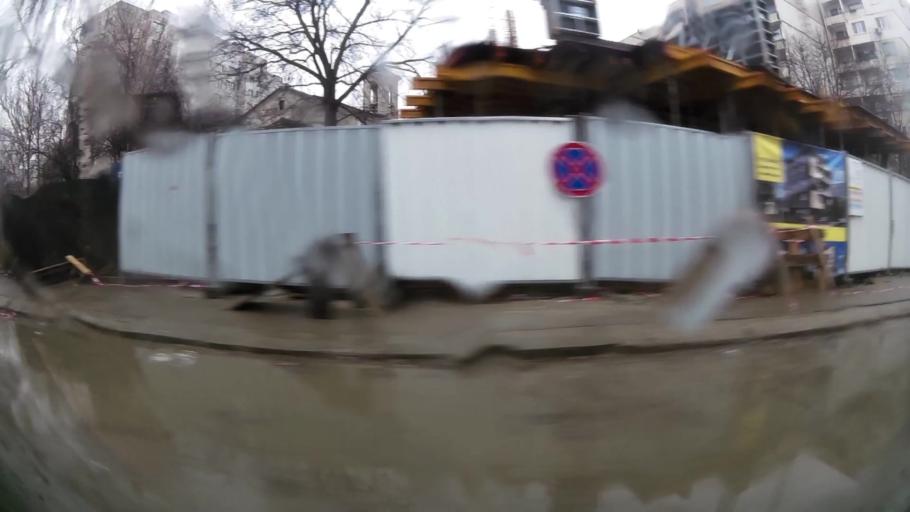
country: BG
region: Sofia-Capital
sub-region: Stolichna Obshtina
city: Sofia
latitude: 42.6533
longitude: 23.3652
